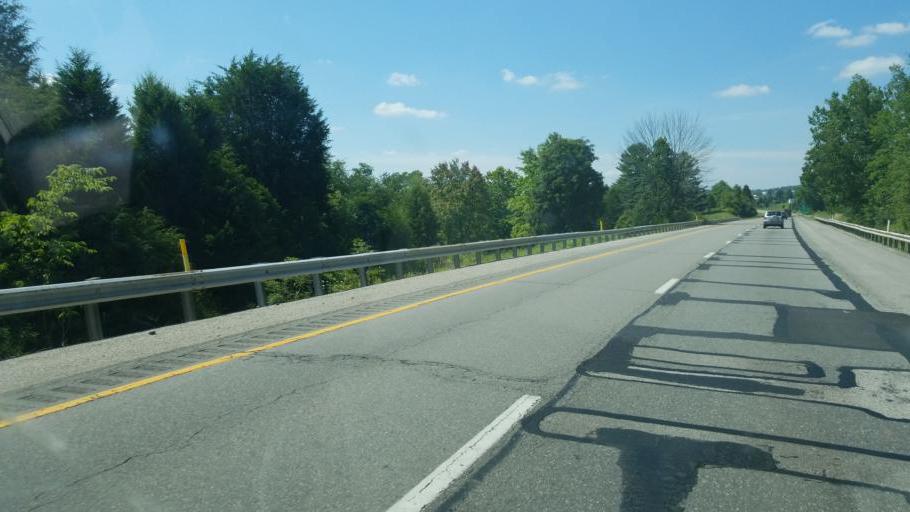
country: US
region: West Virginia
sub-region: Jackson County
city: Ripley
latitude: 38.7497
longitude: -81.6825
